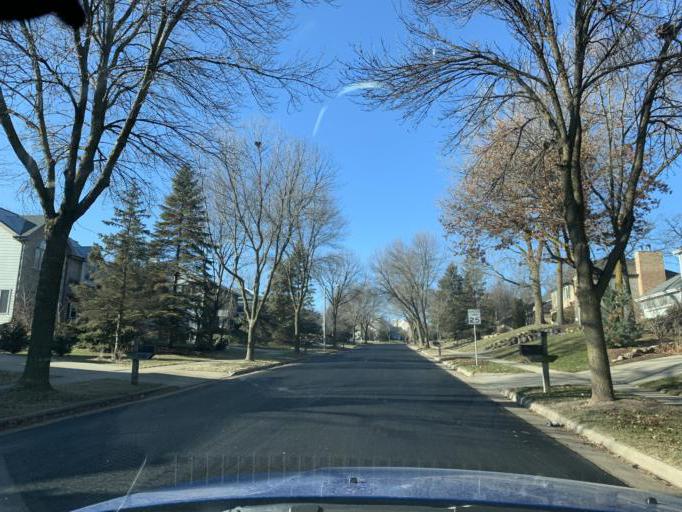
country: US
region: Wisconsin
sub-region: Dane County
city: Middleton
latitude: 43.0446
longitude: -89.5070
